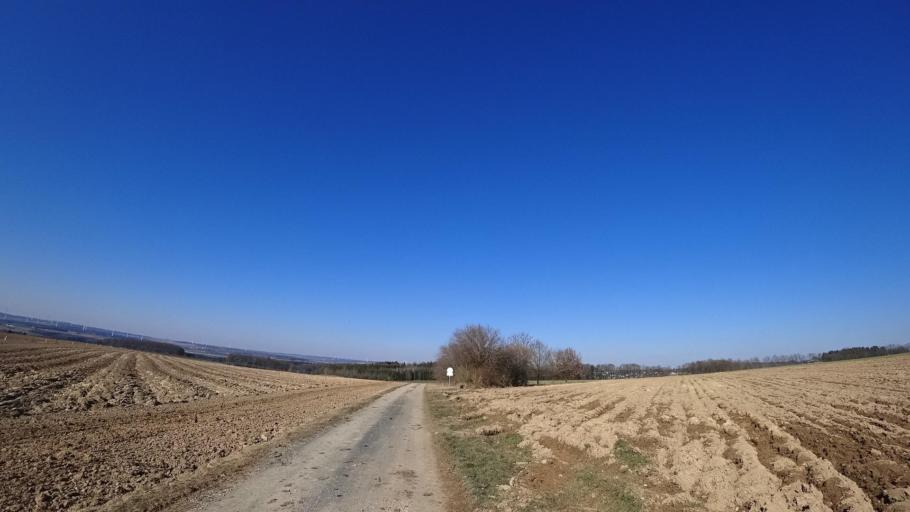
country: DE
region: Rheinland-Pfalz
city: Sargenroth
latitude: 49.9396
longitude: 7.5195
